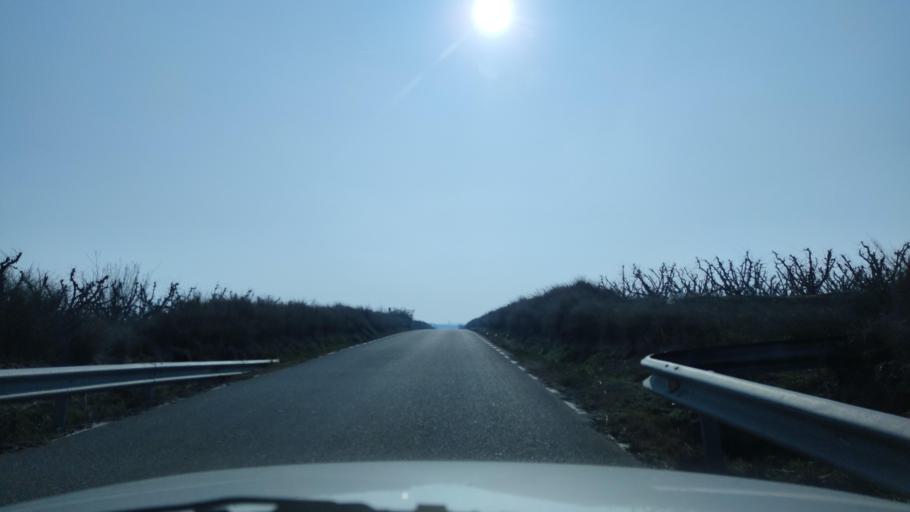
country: ES
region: Catalonia
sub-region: Provincia de Lleida
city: Sunyer
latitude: 41.5401
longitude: 0.5765
